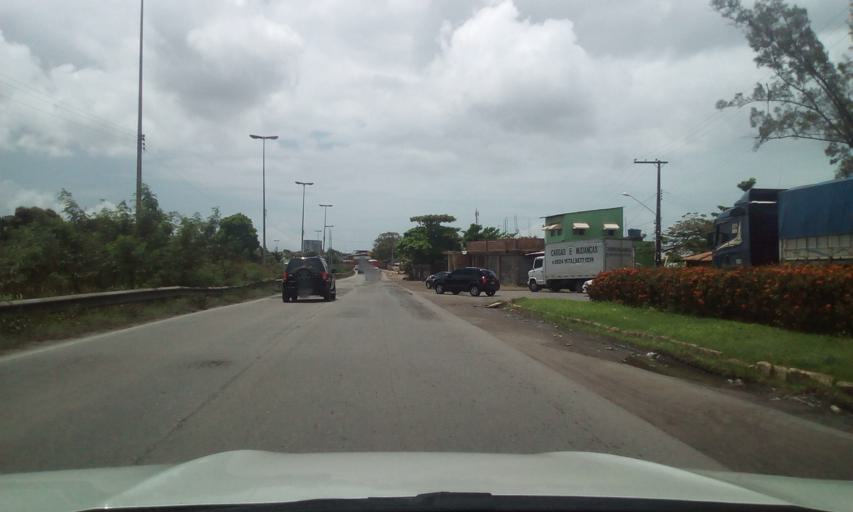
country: BR
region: Pernambuco
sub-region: Recife
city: Recife
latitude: -8.0853
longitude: -34.9454
